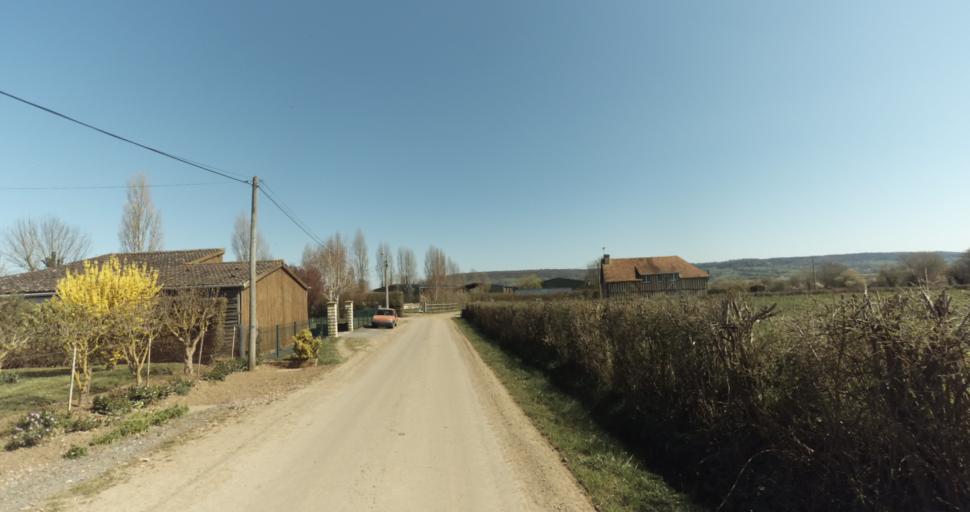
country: FR
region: Lower Normandy
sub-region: Departement du Calvados
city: Saint-Pierre-sur-Dives
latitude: 49.0041
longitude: 0.0008
